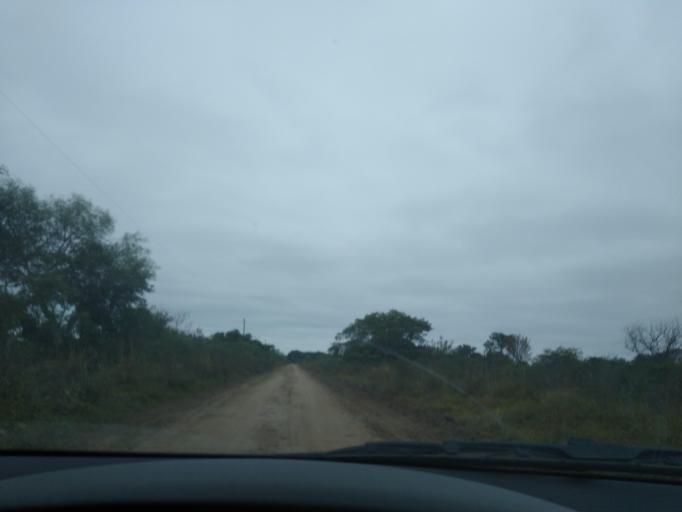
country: AR
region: Chaco
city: Colonia Benitez
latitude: -27.3709
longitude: -58.9477
